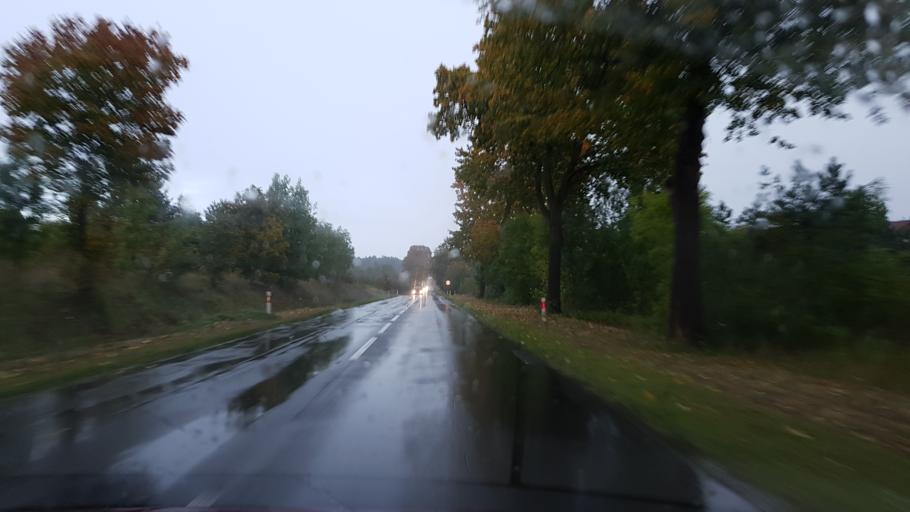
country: PL
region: Greater Poland Voivodeship
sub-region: Powiat pilski
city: Szydlowo
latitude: 53.1577
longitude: 16.6605
